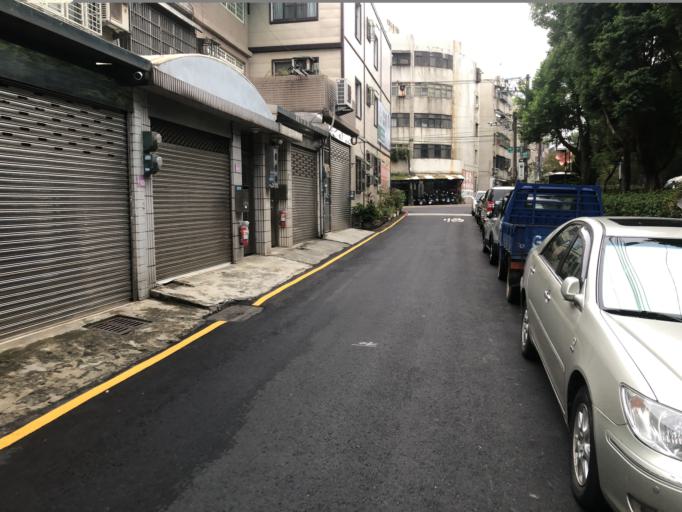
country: TW
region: Taiwan
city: Taoyuan City
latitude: 24.9521
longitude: 121.2361
